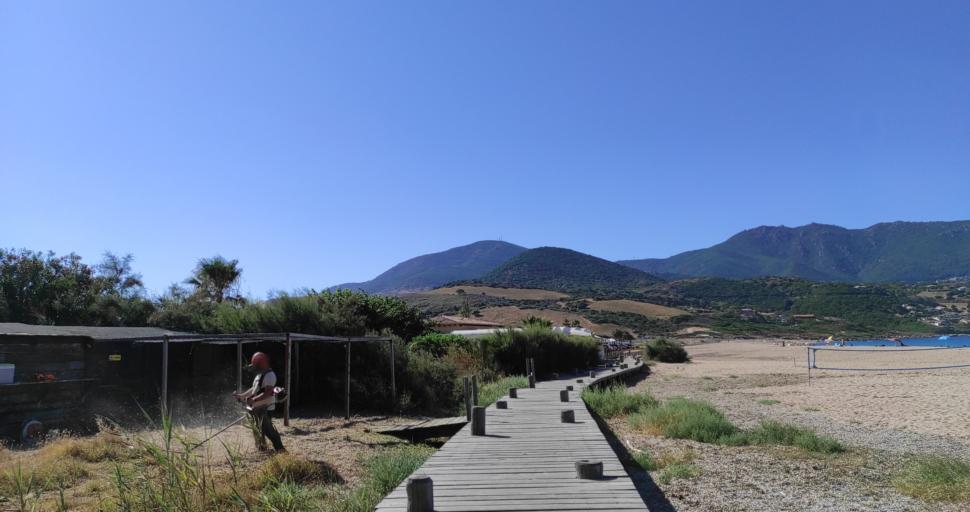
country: FR
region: Corsica
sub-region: Departement de la Corse-du-Sud
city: Alata
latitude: 41.9928
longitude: 8.6689
